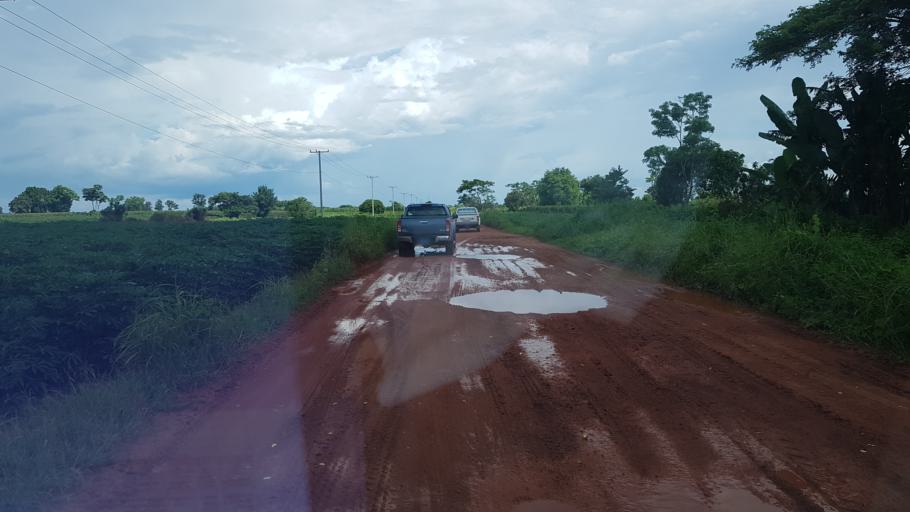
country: LA
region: Vientiane
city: Vientiane
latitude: 18.2321
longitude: 102.5634
